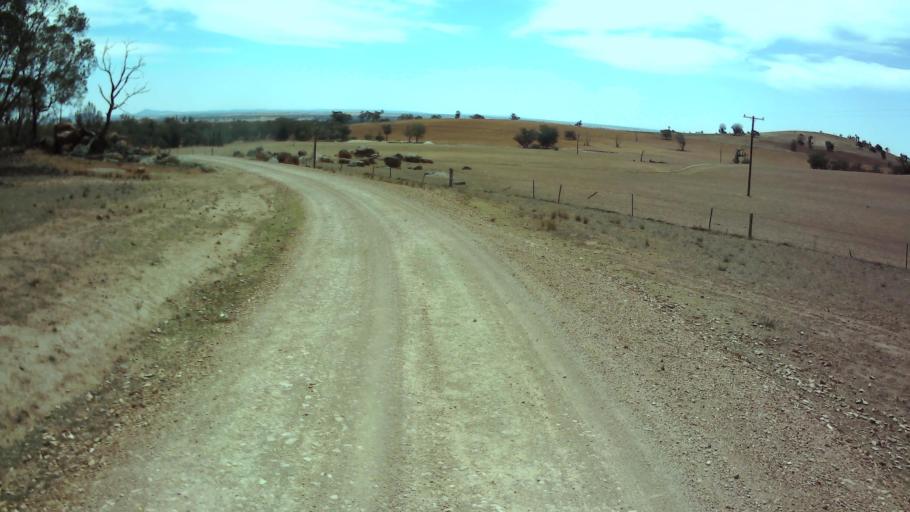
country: AU
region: New South Wales
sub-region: Weddin
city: Grenfell
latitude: -33.7419
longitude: 148.1788
